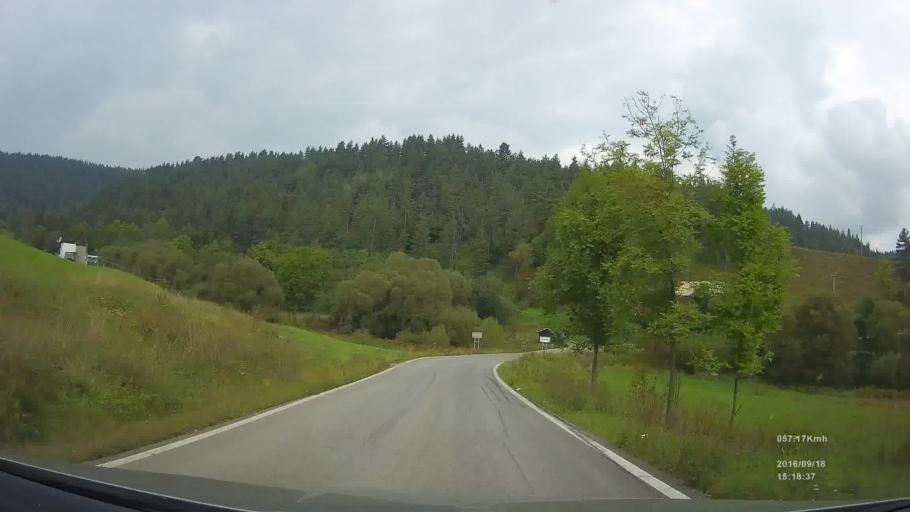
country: SK
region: Presovsky
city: Lubica
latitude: 49.0335
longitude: 20.4886
